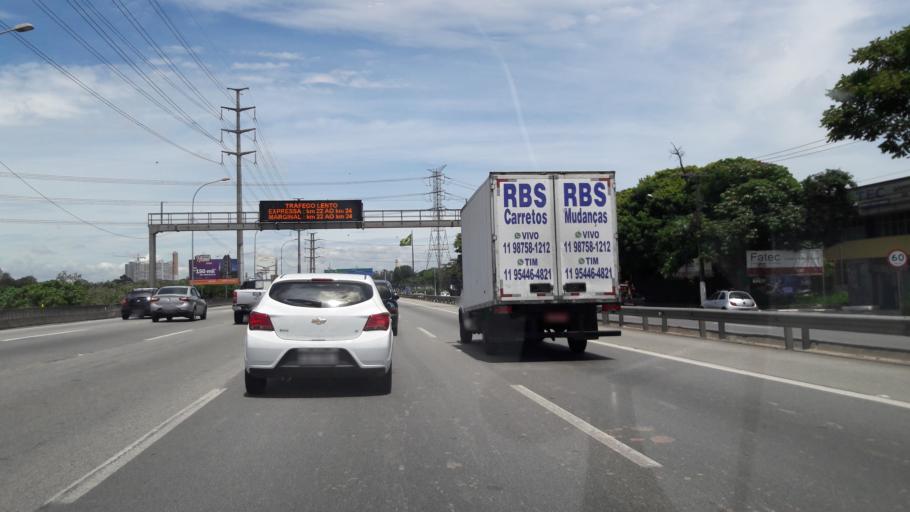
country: BR
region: Sao Paulo
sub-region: Osasco
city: Osasco
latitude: -23.5241
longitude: -46.7584
